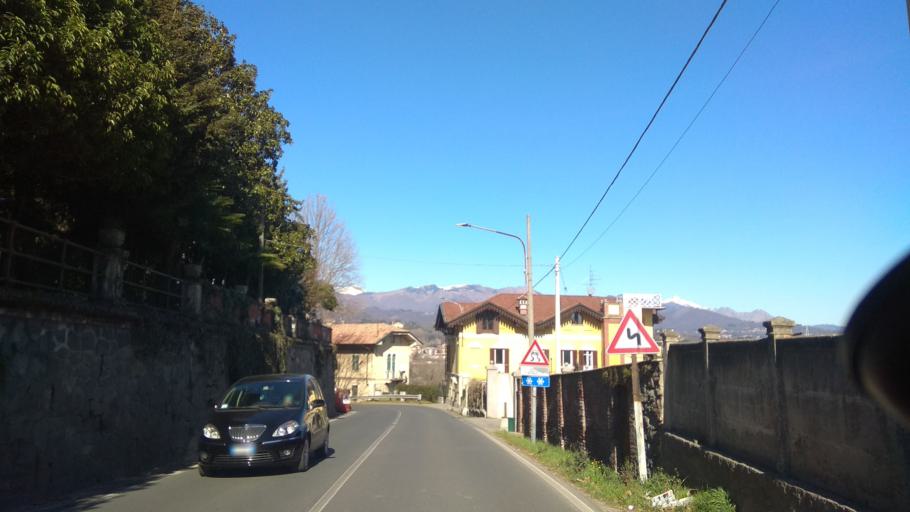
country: IT
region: Piedmont
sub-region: Provincia di Biella
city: Candelo
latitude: 45.5477
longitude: 8.1117
